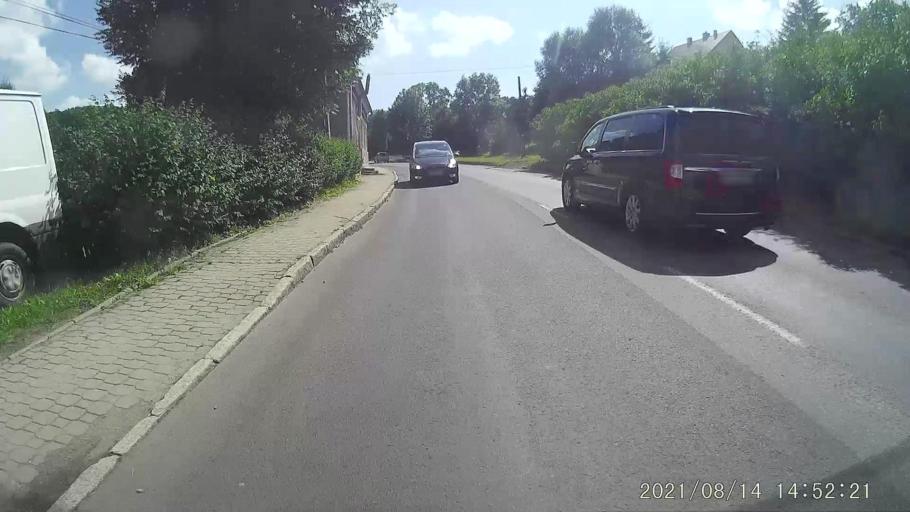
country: PL
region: Lower Silesian Voivodeship
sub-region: Powiat walbrzyski
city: Gluszyca Gorna
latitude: 50.6664
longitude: 16.3758
